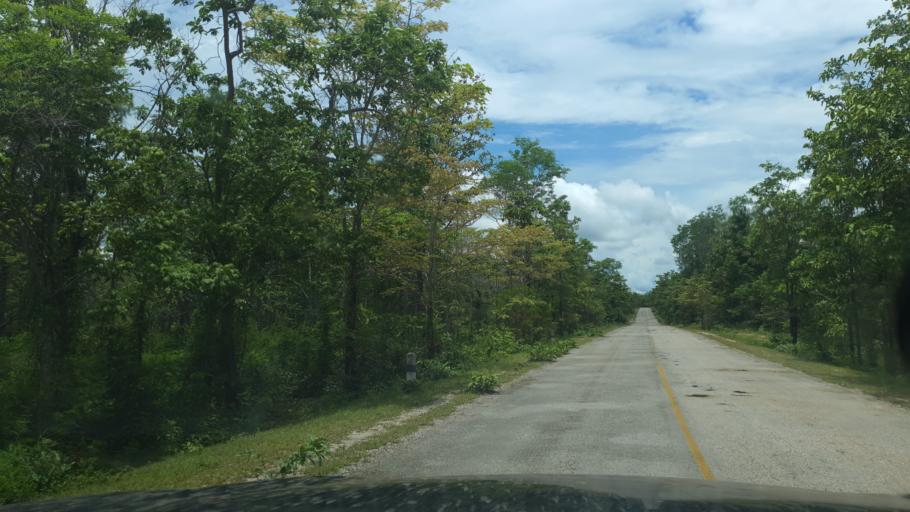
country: TH
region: Lampang
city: Soem Ngam
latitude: 18.0518
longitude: 99.3652
